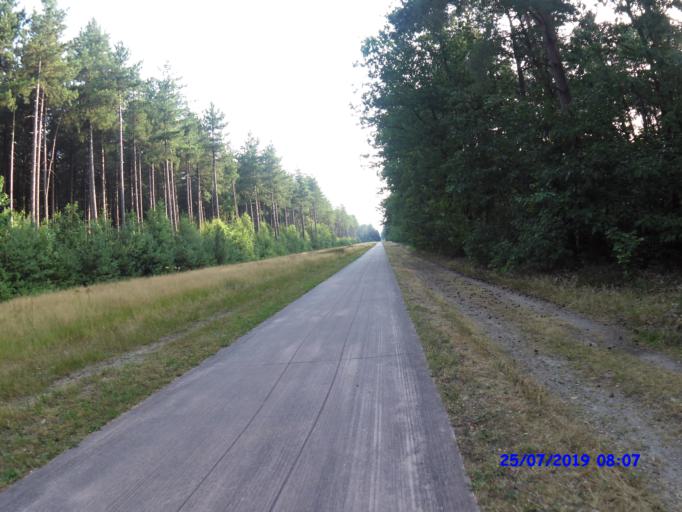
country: BE
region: Flanders
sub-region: Provincie Limburg
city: Lommel
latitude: 51.1694
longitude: 5.3049
